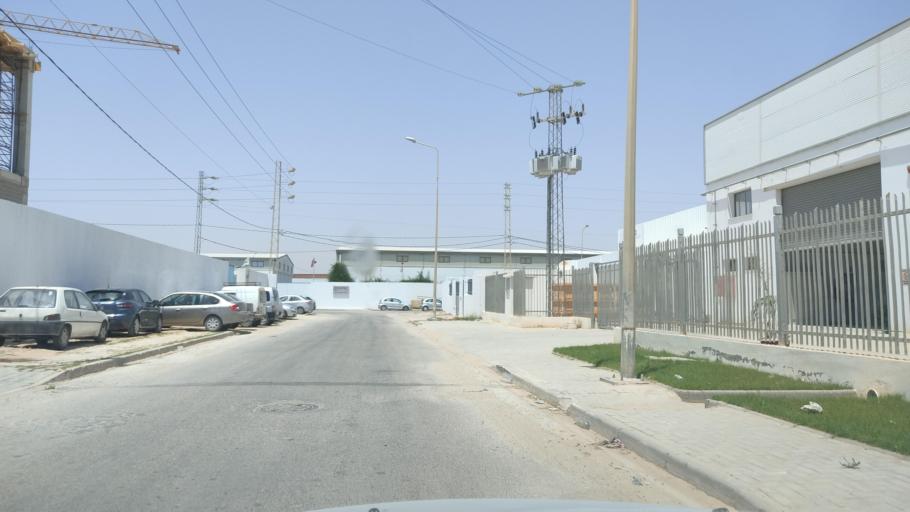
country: TN
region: Safaqis
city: Sfax
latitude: 34.6644
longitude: 10.6971
